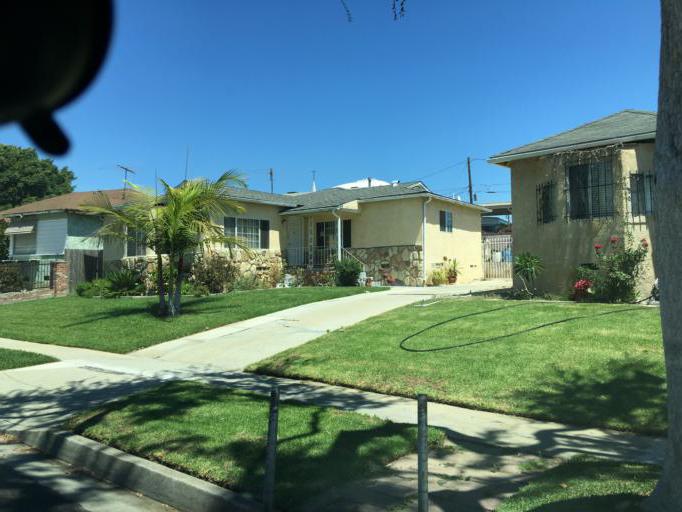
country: US
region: California
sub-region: Los Angeles County
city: Westmont
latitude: 33.9376
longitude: -118.3113
